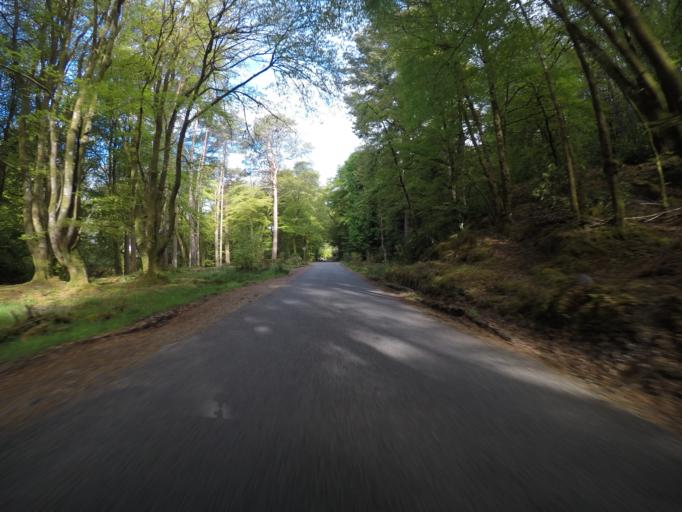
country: GB
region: Scotland
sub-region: Highland
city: Fort William
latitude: 56.6828
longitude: -5.0939
